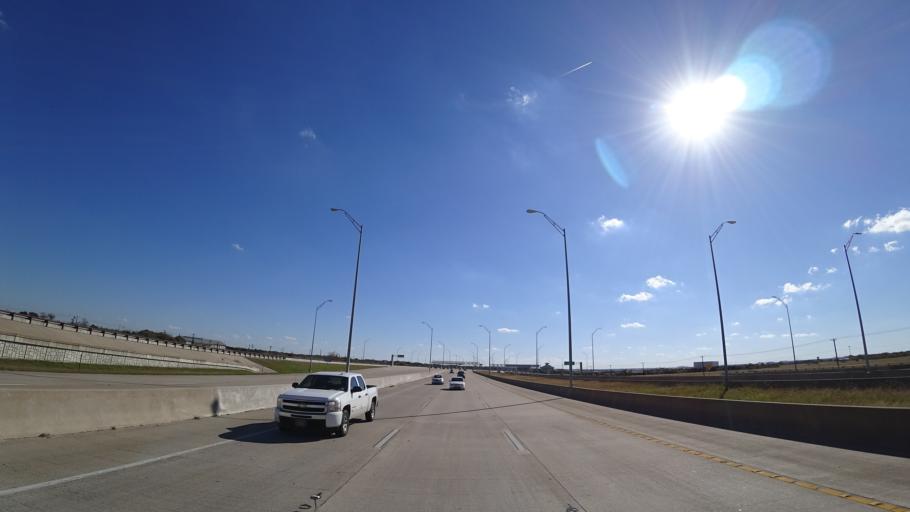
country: US
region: Texas
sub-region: Travis County
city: Wells Branch
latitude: 30.4570
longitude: -97.6978
